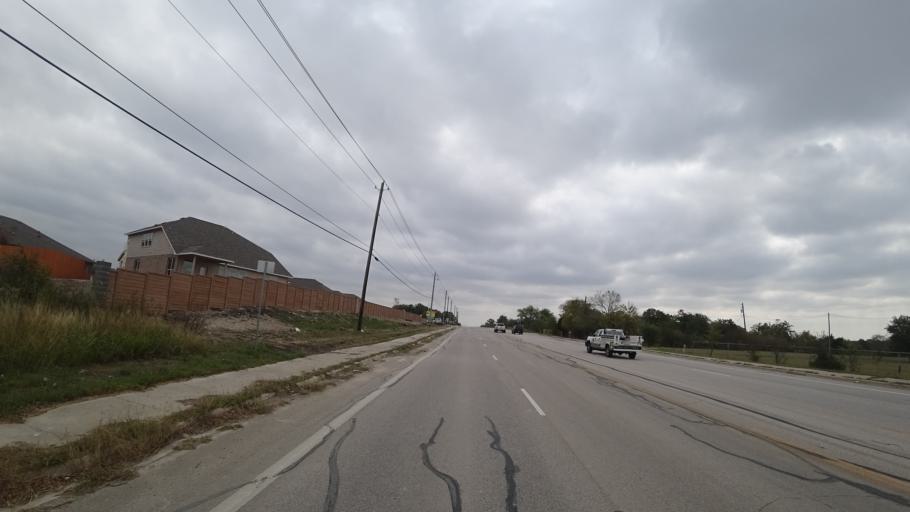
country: US
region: Texas
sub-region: Travis County
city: Pflugerville
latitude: 30.3902
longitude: -97.6242
